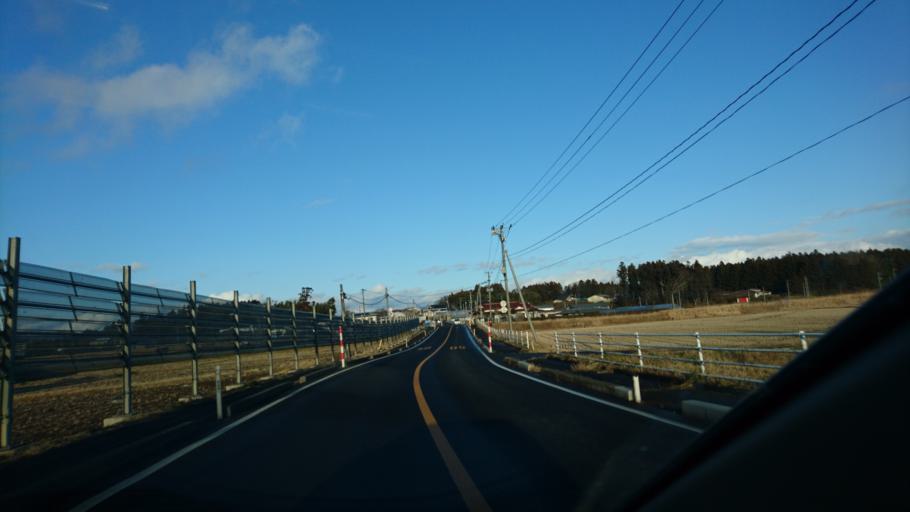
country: JP
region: Miyagi
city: Furukawa
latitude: 38.6004
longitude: 140.8666
